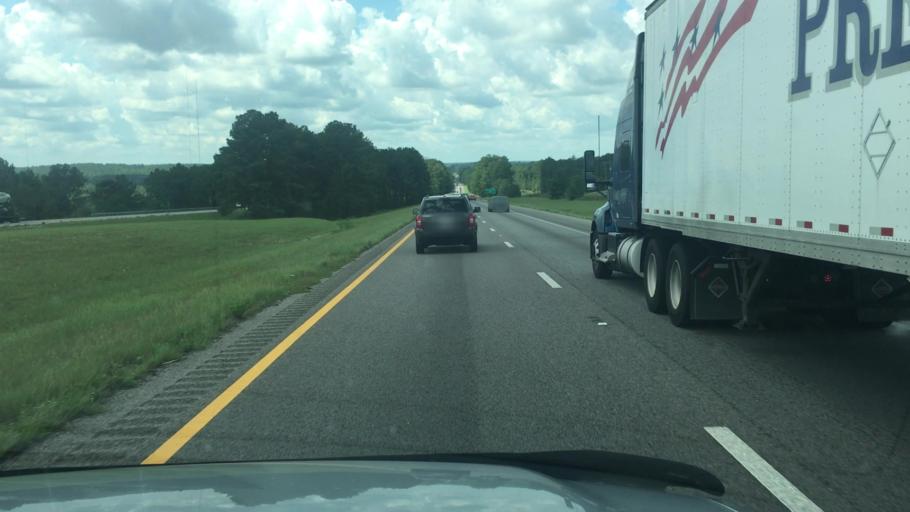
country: US
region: South Carolina
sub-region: Kershaw County
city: Elgin
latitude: 34.1579
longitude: -80.7296
